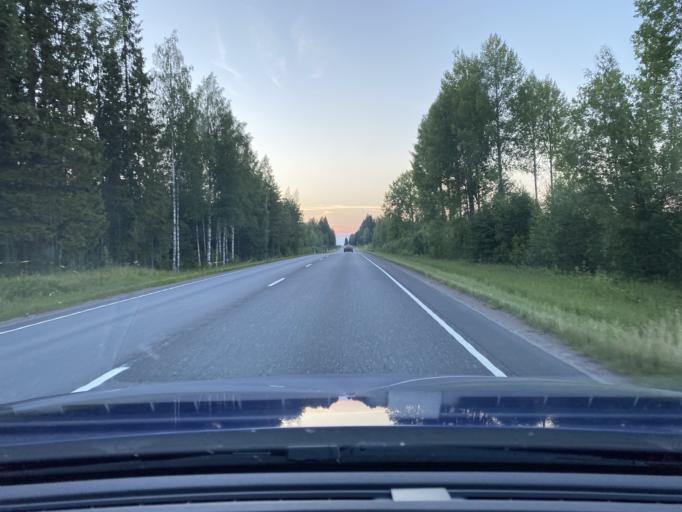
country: FI
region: Pirkanmaa
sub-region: Luoteis-Pirkanmaa
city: Ikaalinen
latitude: 61.8323
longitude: 22.9414
